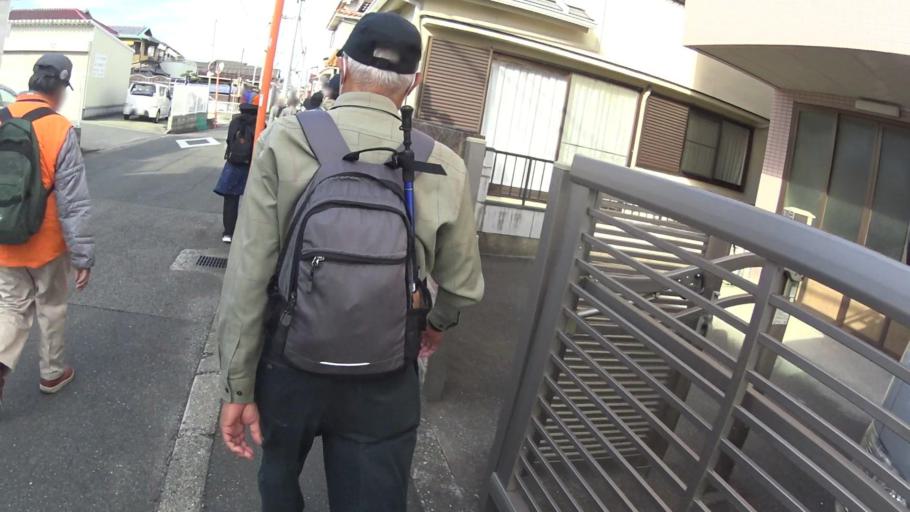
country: JP
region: Osaka
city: Kashihara
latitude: 34.5805
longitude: 135.5911
